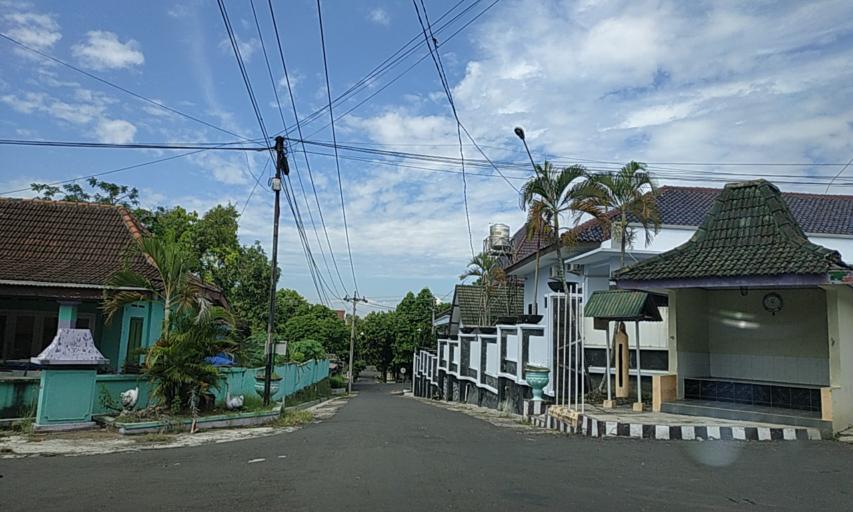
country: ID
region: Central Java
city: Selogiri
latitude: -7.8145
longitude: 110.9280
